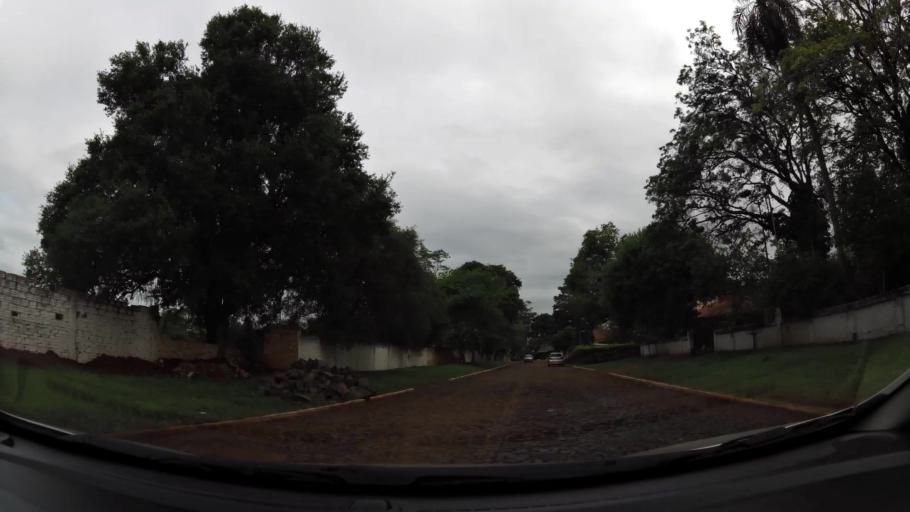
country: PY
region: Alto Parana
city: Ciudad del Este
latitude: -25.4084
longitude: -54.6404
